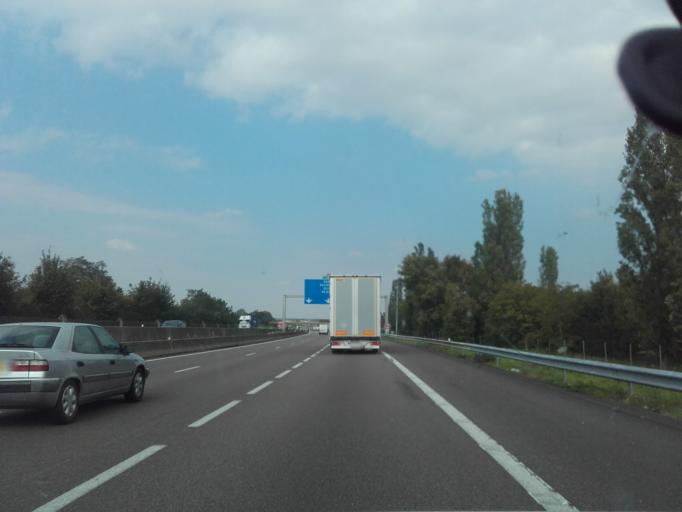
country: FR
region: Bourgogne
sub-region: Departement de Saone-et-Loire
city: Chatenoy-le-Royal
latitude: 46.7993
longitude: 4.8245
